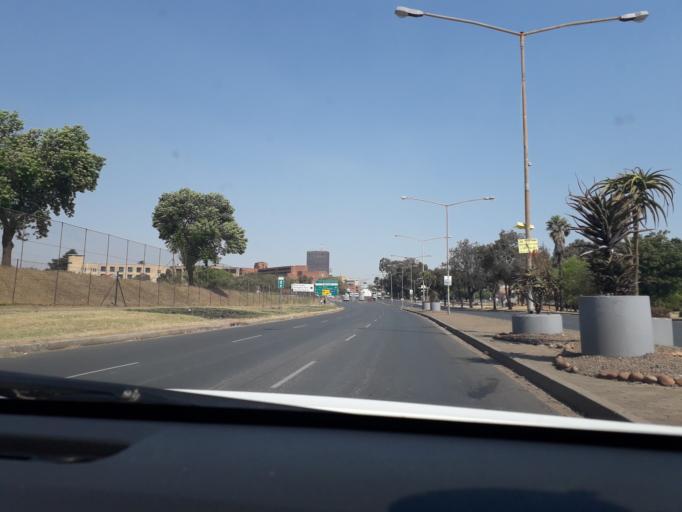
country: ZA
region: Gauteng
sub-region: City of Johannesburg Metropolitan Municipality
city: Modderfontein
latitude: -26.0990
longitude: 28.2236
